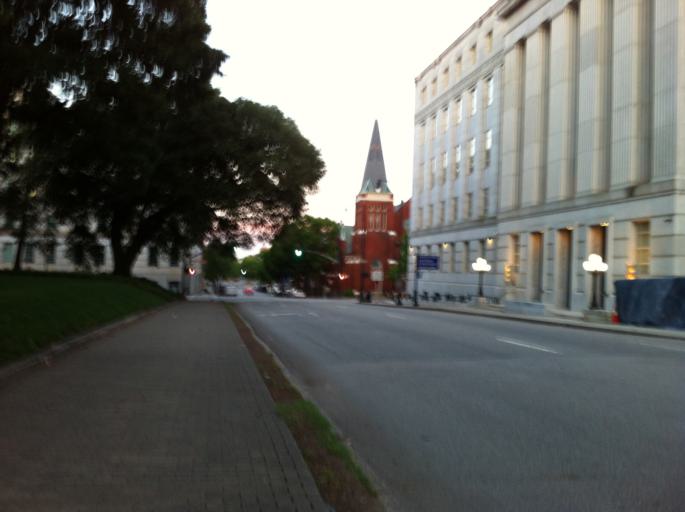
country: US
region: North Carolina
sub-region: Wake County
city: Raleigh
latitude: 35.7796
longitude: -78.6390
